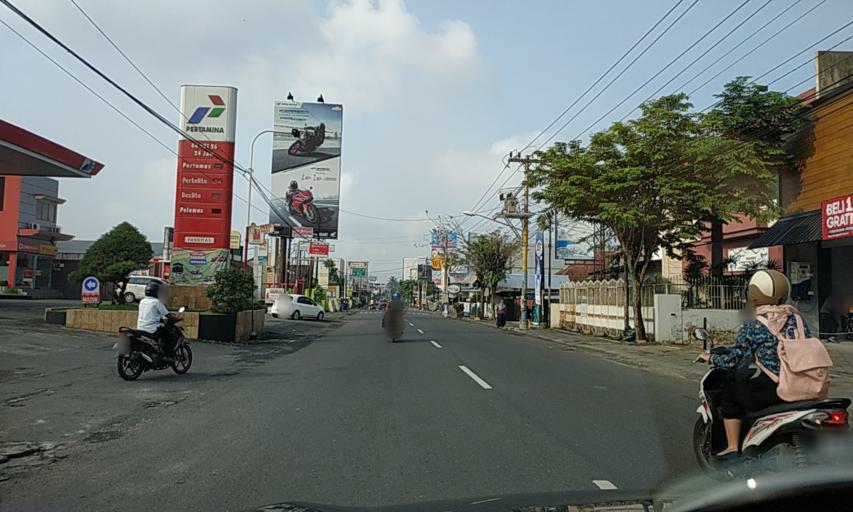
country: ID
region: Central Java
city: Purwokerto
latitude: -7.4214
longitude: 109.2442
